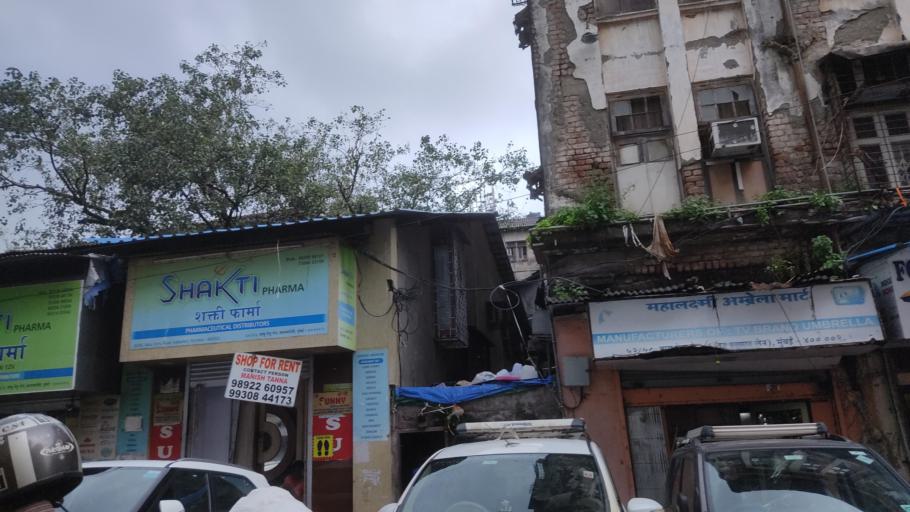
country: IN
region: Maharashtra
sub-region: Raigarh
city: Uran
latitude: 18.9477
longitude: 72.8297
